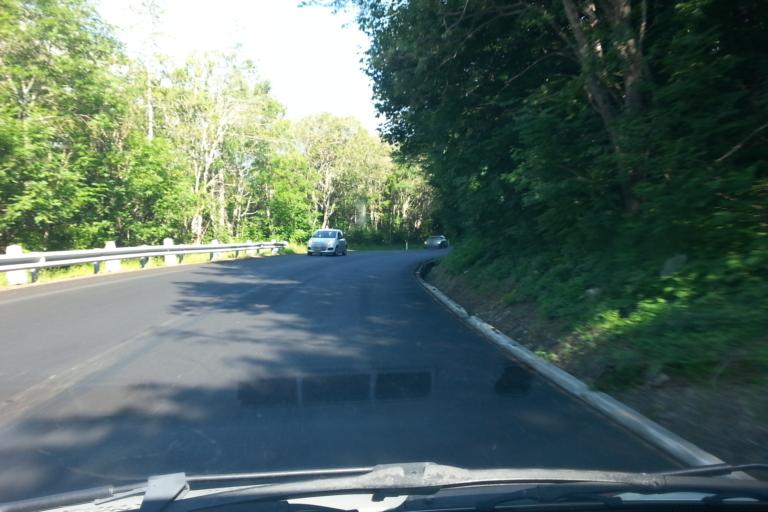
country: IT
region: Piedmont
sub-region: Provincia di Torino
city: Moncenisio
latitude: 45.1847
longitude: 6.9855
